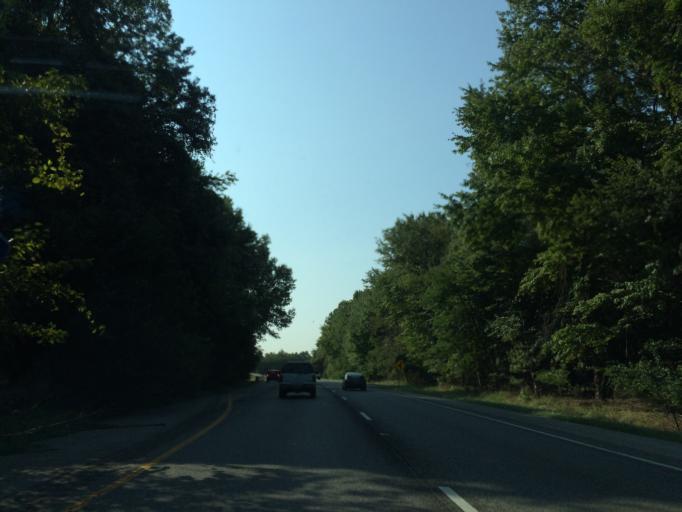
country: US
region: Maryland
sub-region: Prince George's County
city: Mitchellville
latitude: 38.8907
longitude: -76.7216
